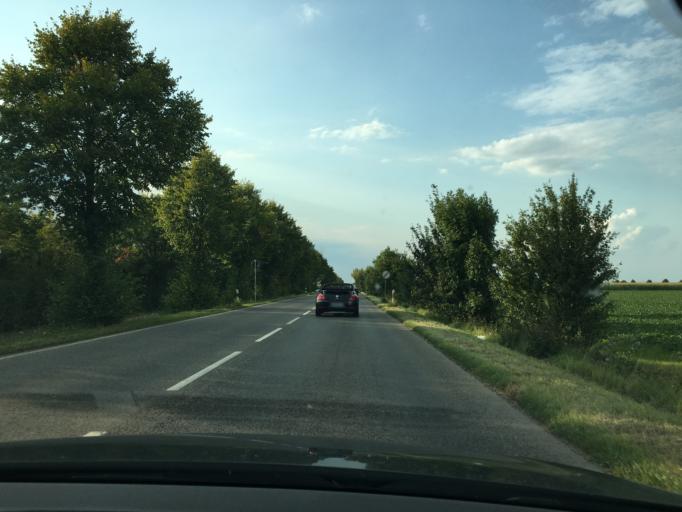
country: DE
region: North Rhine-Westphalia
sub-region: Regierungsbezirk Koln
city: Merzenich
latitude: 50.8184
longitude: 6.5473
